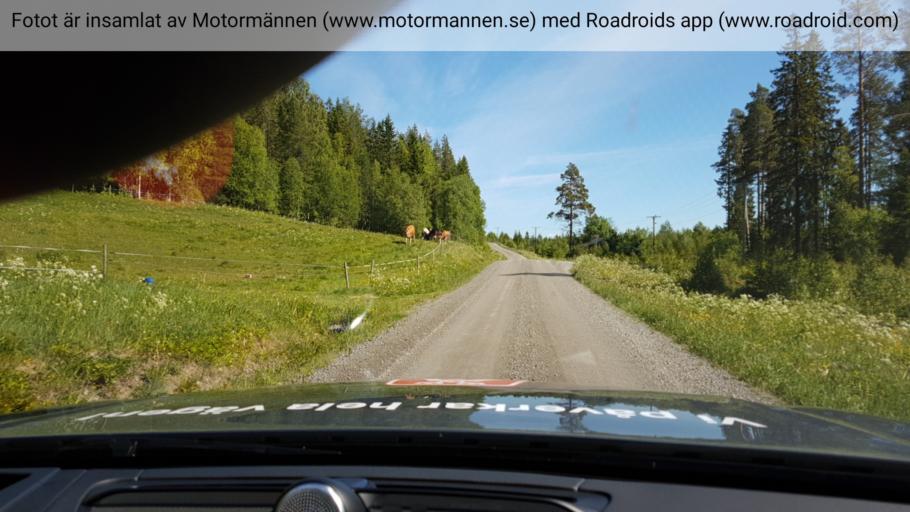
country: SE
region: Jaemtland
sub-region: OEstersunds Kommun
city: Brunflo
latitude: 62.9682
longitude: 14.6954
